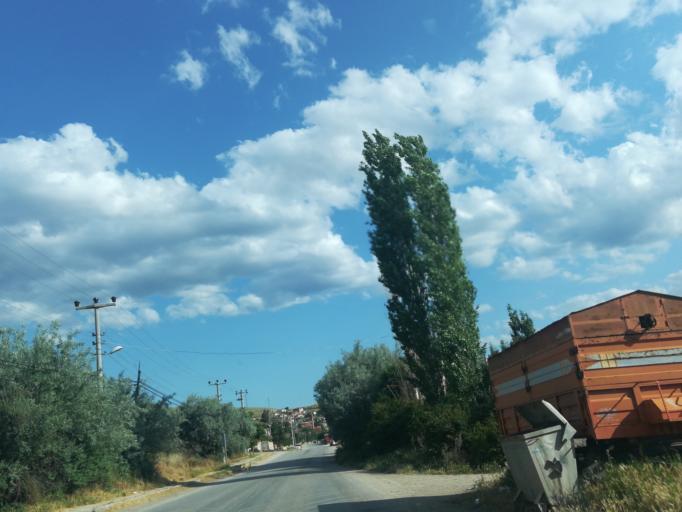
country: TR
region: Afyonkarahisar
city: Dinar
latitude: 38.0812
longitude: 30.1674
